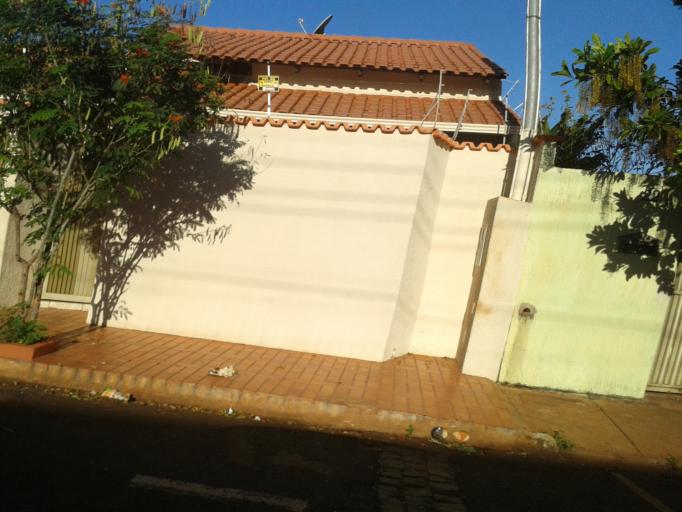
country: BR
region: Minas Gerais
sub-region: Centralina
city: Centralina
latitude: -18.7261
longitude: -49.2065
